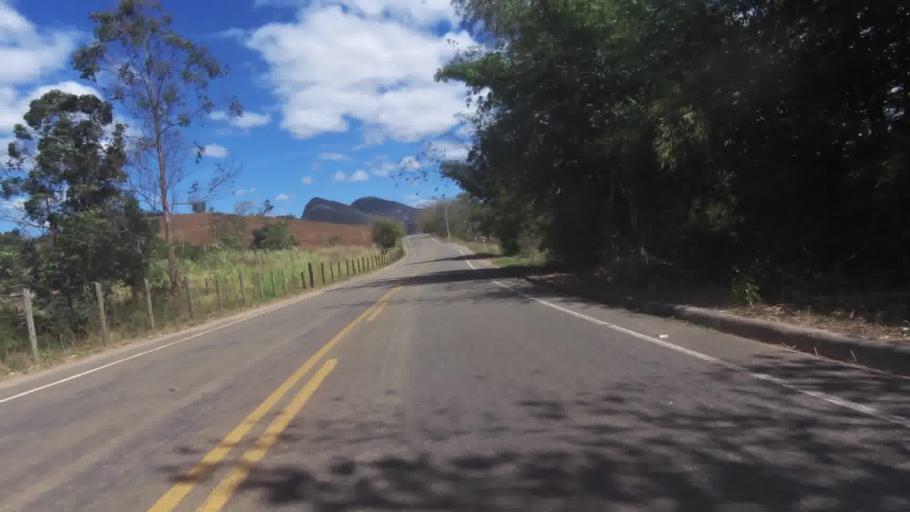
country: BR
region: Espirito Santo
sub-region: Cachoeiro De Itapemirim
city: Cachoeiro de Itapemirim
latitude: -20.9134
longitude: -41.2162
